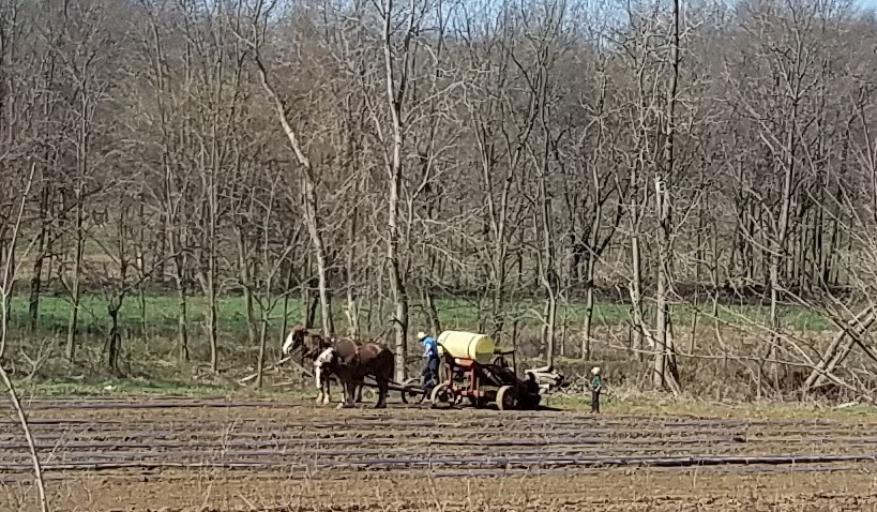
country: US
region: Ohio
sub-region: Knox County
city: Fredericktown
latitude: 40.5398
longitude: -82.6356
